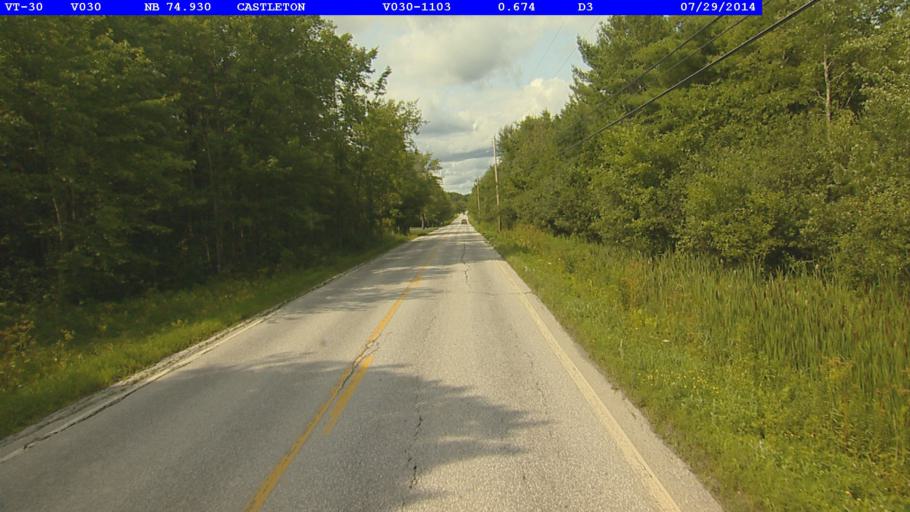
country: US
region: Vermont
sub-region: Rutland County
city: Castleton
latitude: 43.5965
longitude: -73.2091
